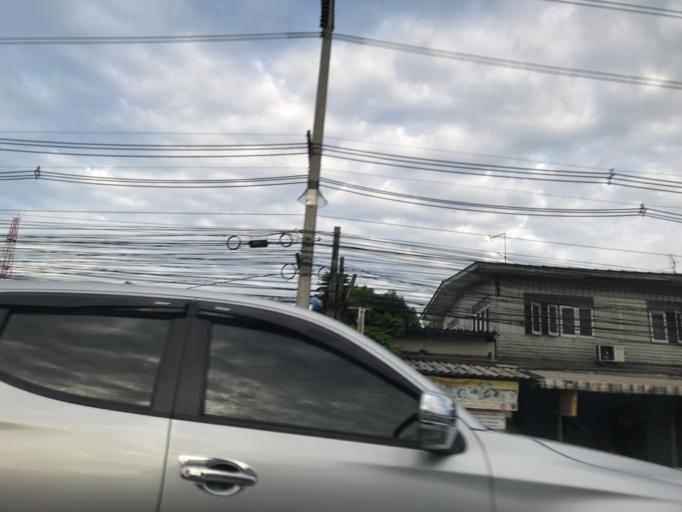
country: TH
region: Chon Buri
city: Bang Lamung
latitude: 13.0219
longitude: 100.9313
